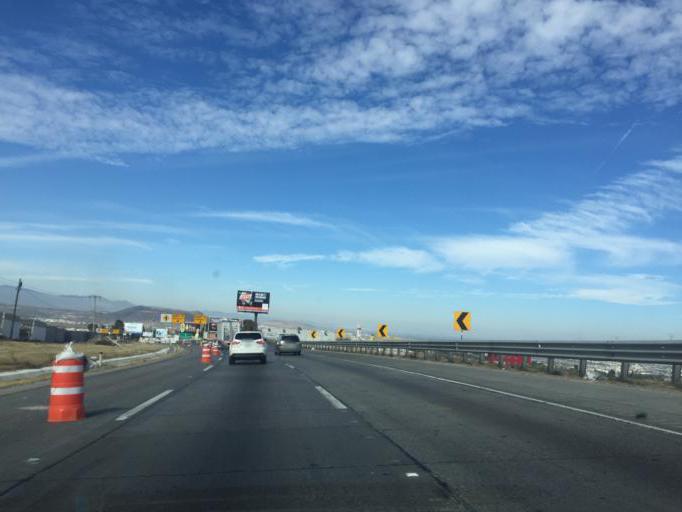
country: MX
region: Queretaro
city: San Juan del Rio
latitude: 20.3617
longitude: -99.9652
